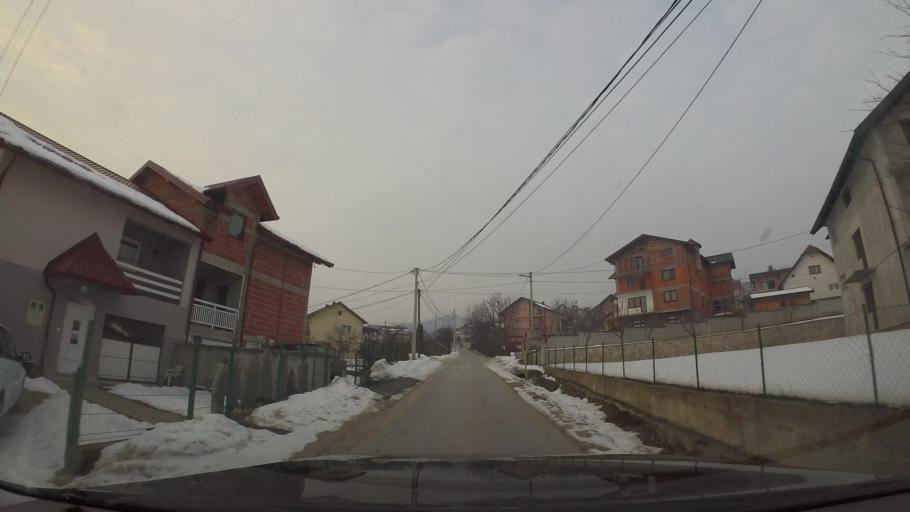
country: BA
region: Federation of Bosnia and Herzegovina
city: Vogosca
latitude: 43.9034
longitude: 18.3533
